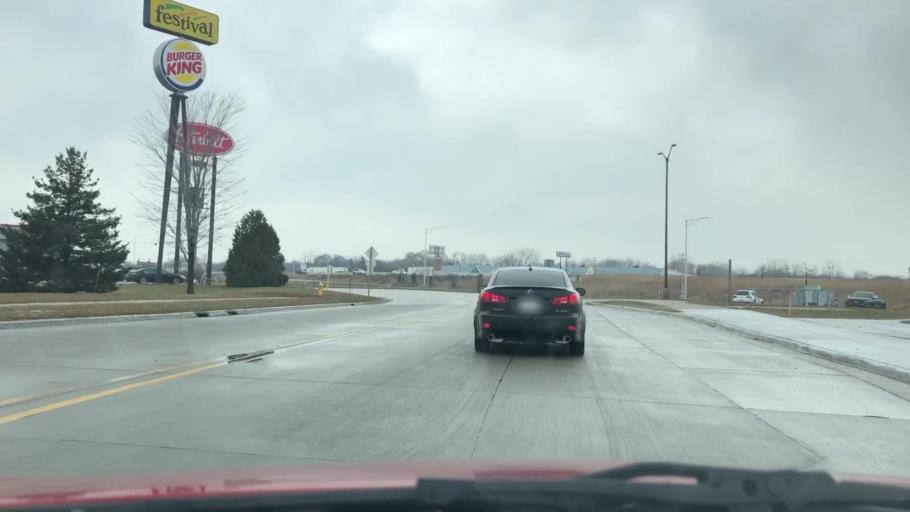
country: US
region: Wisconsin
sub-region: Brown County
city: De Pere
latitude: 44.4513
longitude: -88.0882
